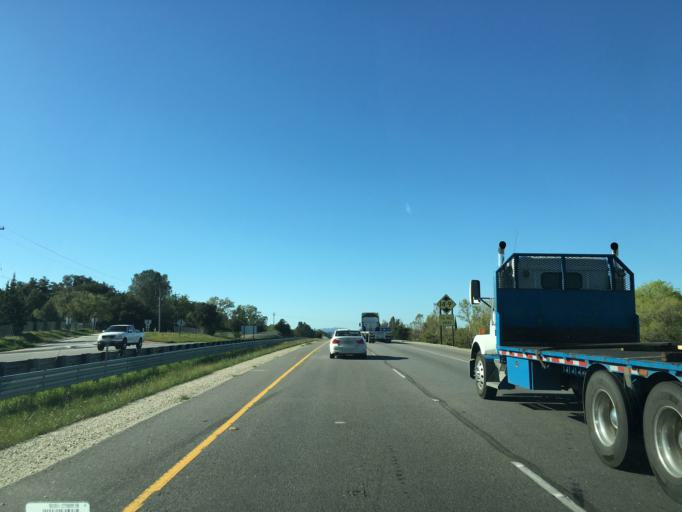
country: US
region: California
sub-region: San Luis Obispo County
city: Atascadero
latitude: 35.4564
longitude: -120.6438
